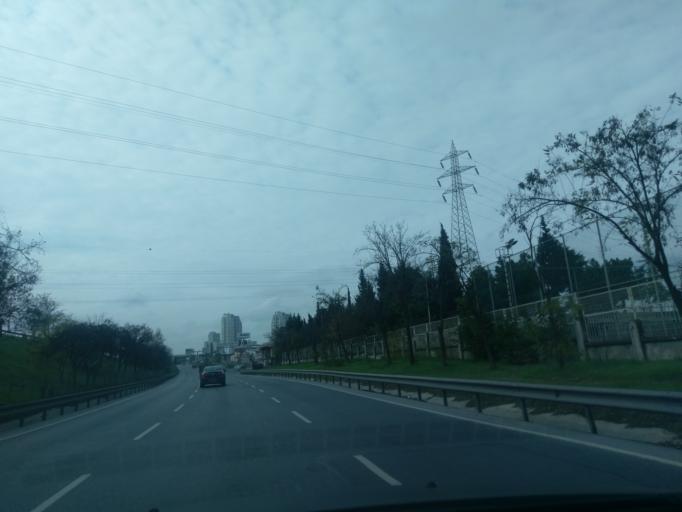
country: TR
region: Istanbul
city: Basaksehir
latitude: 41.0645
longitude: 28.7926
